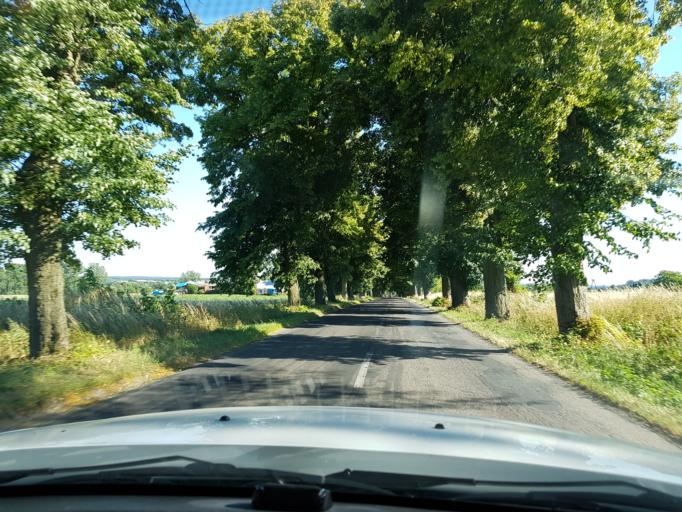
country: PL
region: West Pomeranian Voivodeship
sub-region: Powiat lobeski
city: Lobez
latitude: 53.6521
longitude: 15.6134
